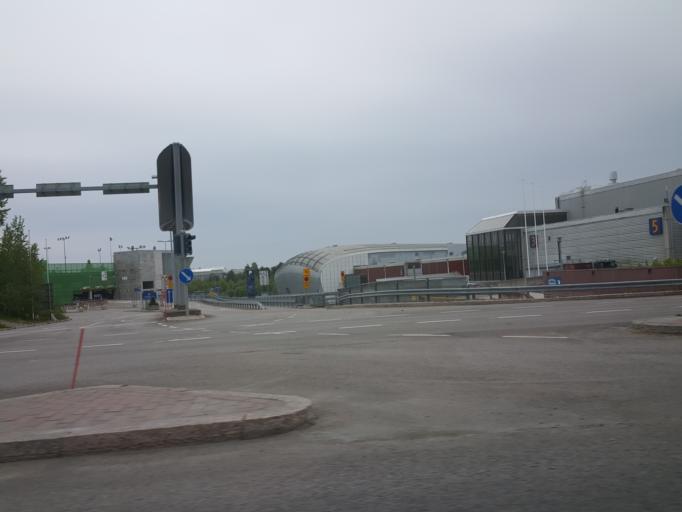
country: FI
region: Uusimaa
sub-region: Helsinki
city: Helsinki
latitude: 60.2041
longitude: 24.9328
